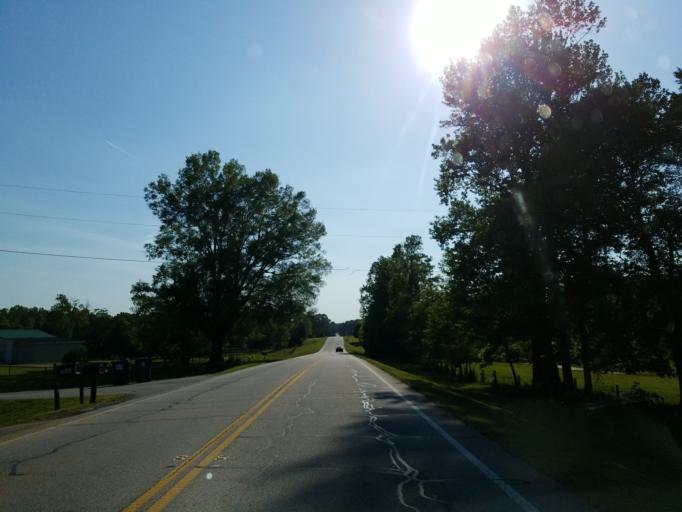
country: US
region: Georgia
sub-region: Carroll County
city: Villa Rica
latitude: 33.8517
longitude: -84.9460
